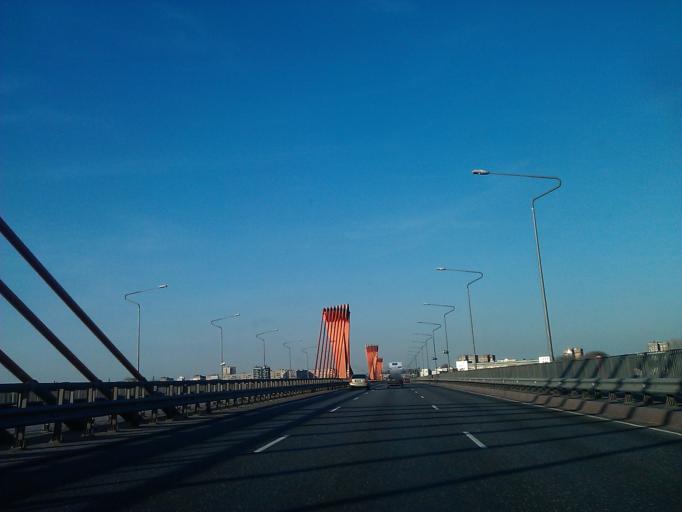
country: LV
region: Kekava
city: Balozi
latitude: 56.9154
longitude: 24.1568
